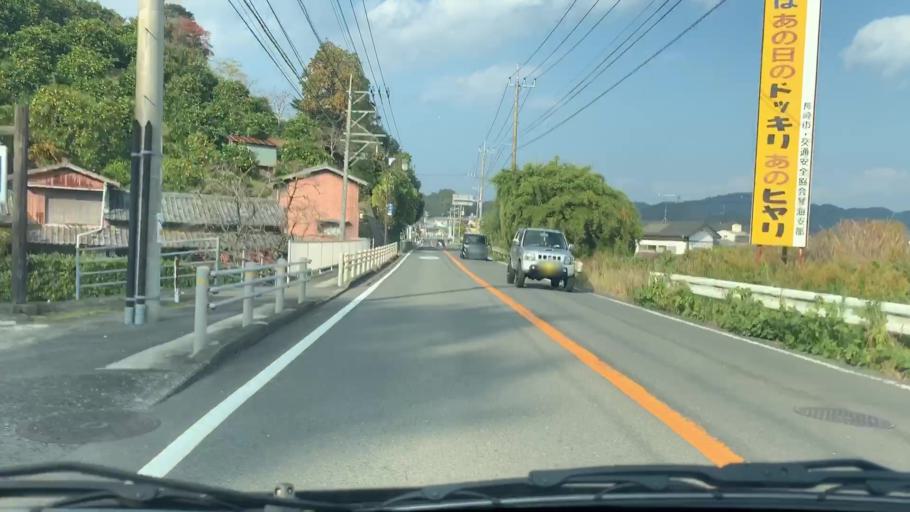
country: JP
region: Nagasaki
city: Togitsu
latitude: 32.9419
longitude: 129.7820
